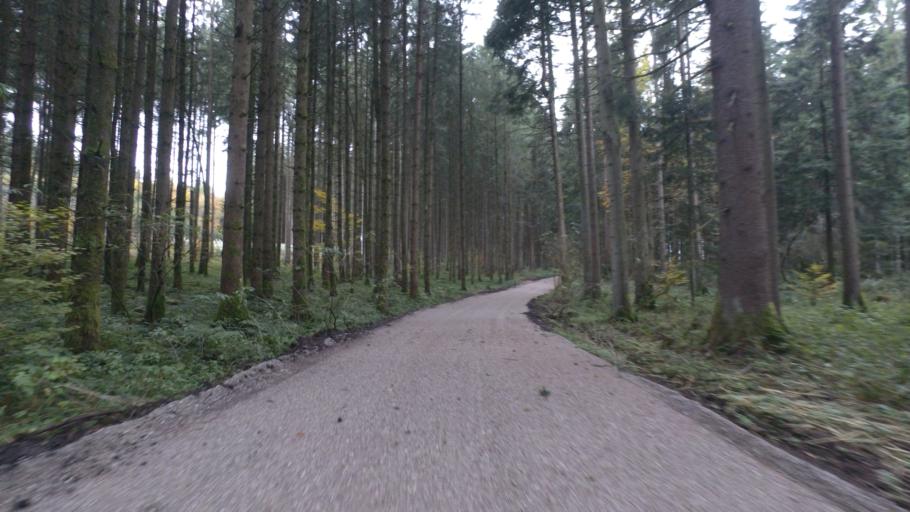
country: DE
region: Bavaria
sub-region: Upper Bavaria
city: Nussdorf
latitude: 47.9102
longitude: 12.5769
